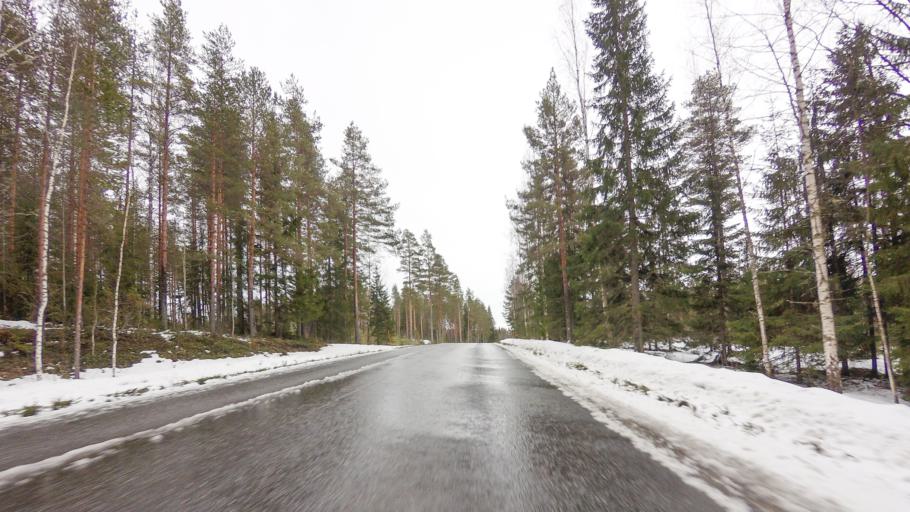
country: FI
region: Southern Savonia
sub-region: Savonlinna
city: Savonlinna
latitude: 61.9788
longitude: 28.8130
